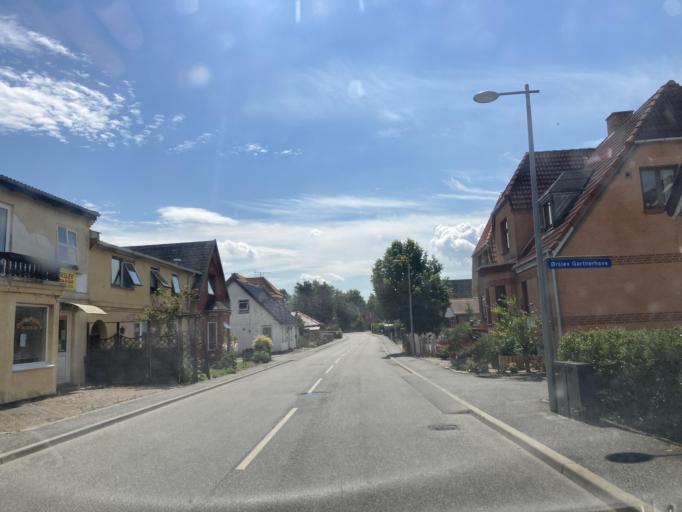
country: DK
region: Zealand
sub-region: Faxe Kommune
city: Haslev
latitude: 55.3885
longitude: 11.9386
